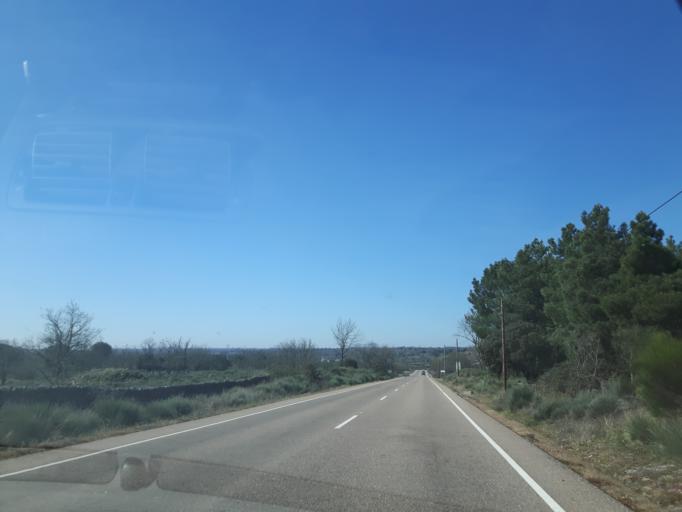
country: ES
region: Castille and Leon
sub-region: Provincia de Salamanca
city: Bermellar
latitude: 40.9636
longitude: -6.6408
